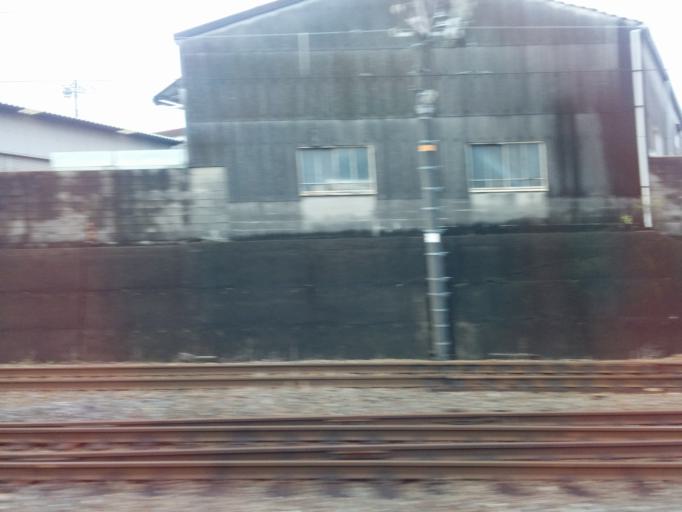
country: JP
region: Shiga Prefecture
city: Otsu-shi
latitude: 34.9954
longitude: 135.8841
